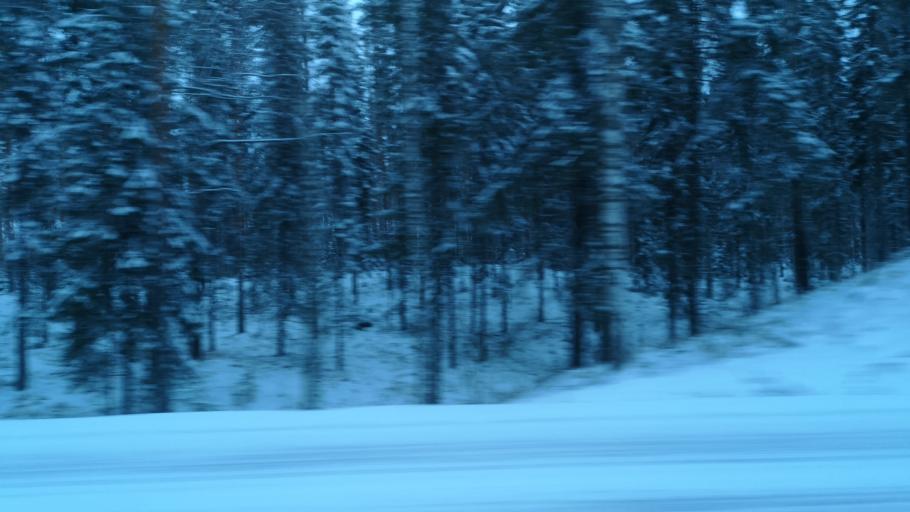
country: FI
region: Southern Savonia
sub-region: Savonlinna
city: Savonlinna
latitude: 61.9828
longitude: 28.8085
